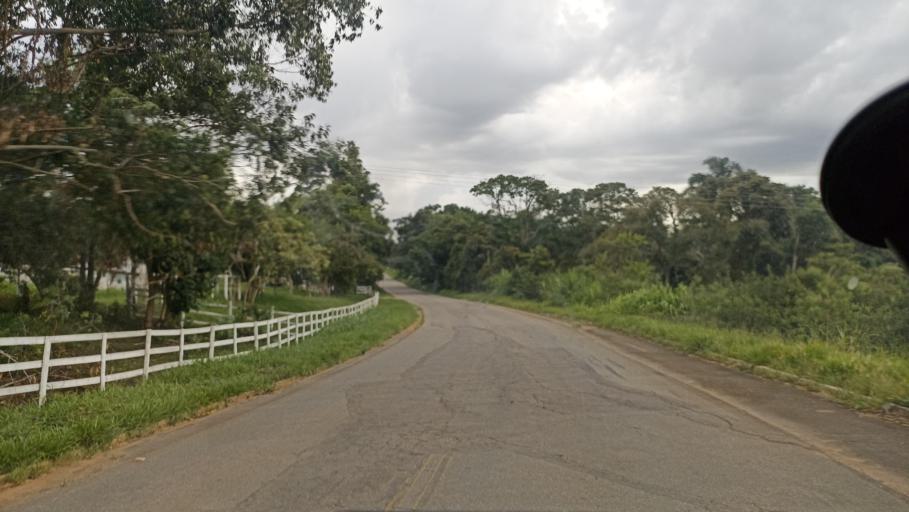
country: BR
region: Minas Gerais
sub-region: Cruzilia
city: Cruzilia
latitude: -21.9056
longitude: -44.8215
